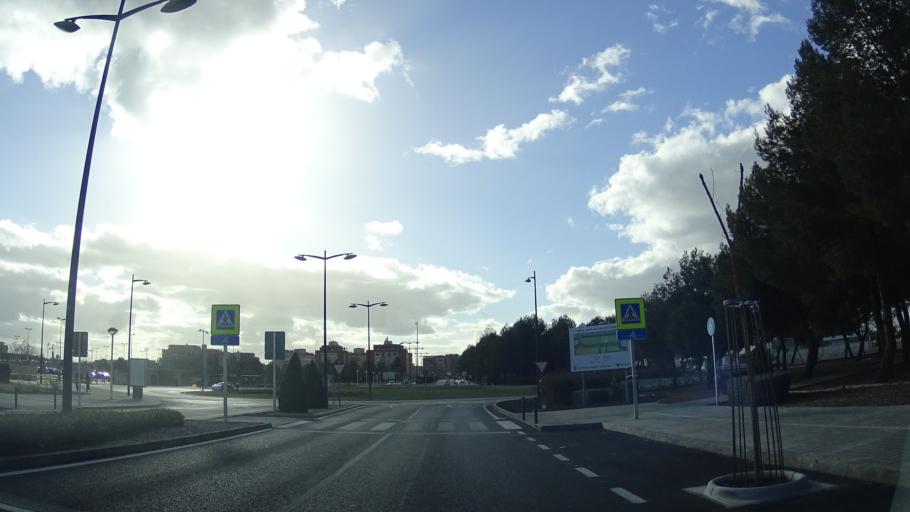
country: ES
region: Castille-La Mancha
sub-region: Provincia de Ciudad Real
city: Ciudad Real
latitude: 38.9730
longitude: -3.9304
